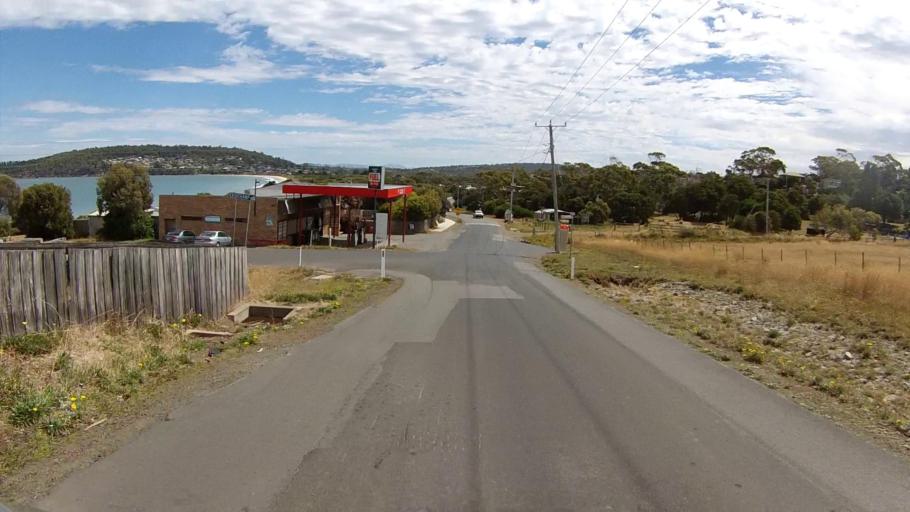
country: AU
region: Tasmania
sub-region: Sorell
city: Sorell
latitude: -42.8938
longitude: 147.6720
